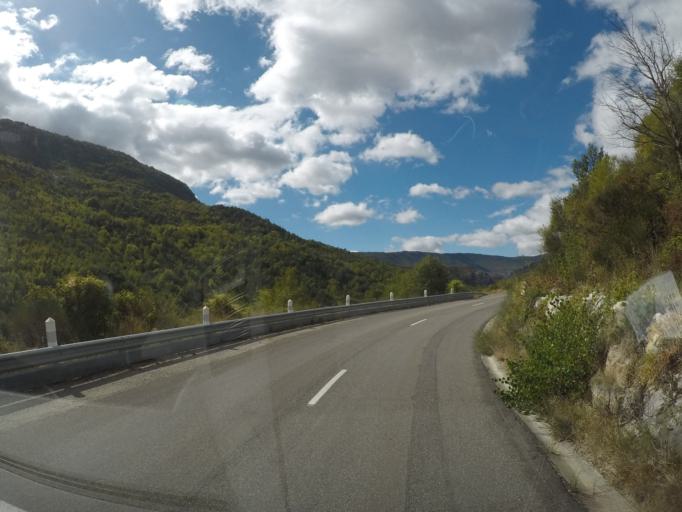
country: FR
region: Provence-Alpes-Cote d'Azur
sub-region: Departement des Hautes-Alpes
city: Laragne-Monteglin
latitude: 44.1762
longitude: 5.6586
